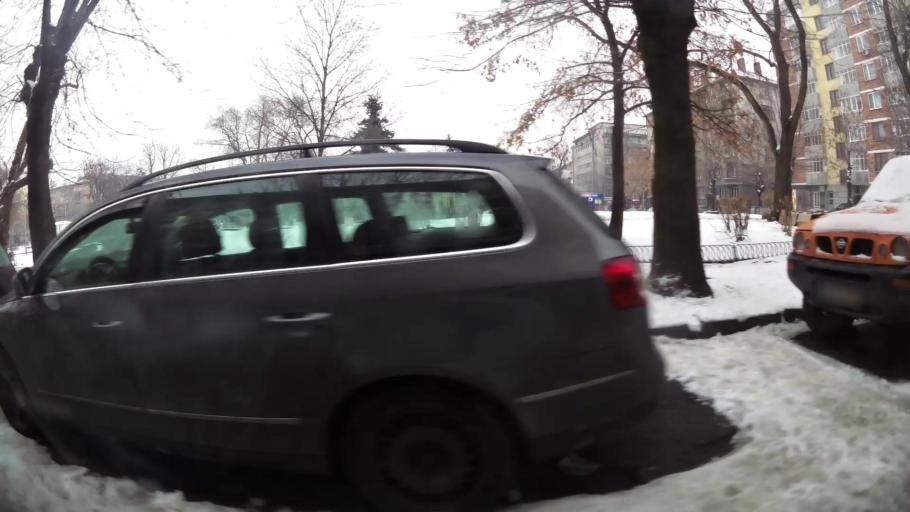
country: BG
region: Sofia-Capital
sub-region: Stolichna Obshtina
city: Sofia
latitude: 42.7084
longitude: 23.3170
